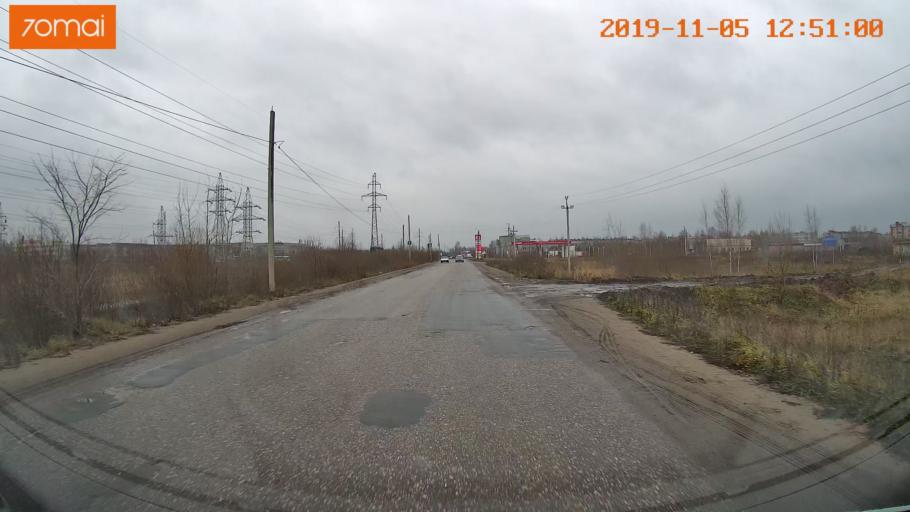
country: RU
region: Ivanovo
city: Kokhma
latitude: 56.9468
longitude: 41.1101
